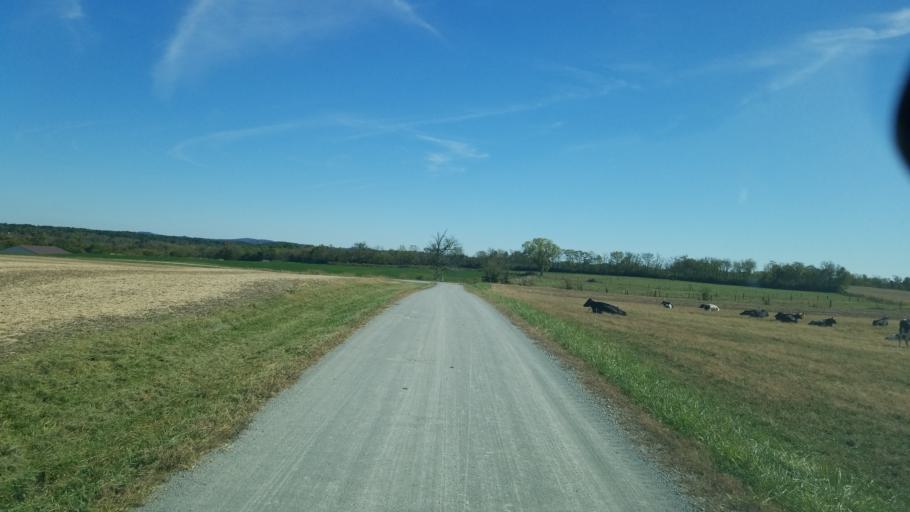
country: US
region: Ohio
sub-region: Highland County
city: Leesburg
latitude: 39.2940
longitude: -83.4722
